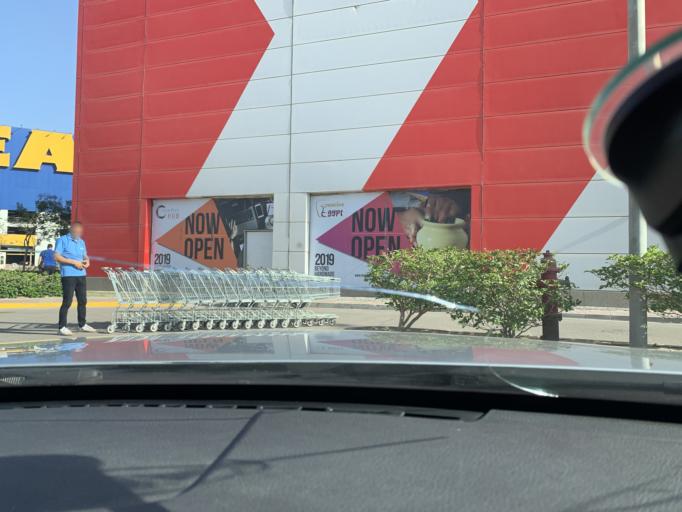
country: EG
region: Muhafazat al Qahirah
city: Cairo
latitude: 30.0316
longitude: 31.4062
